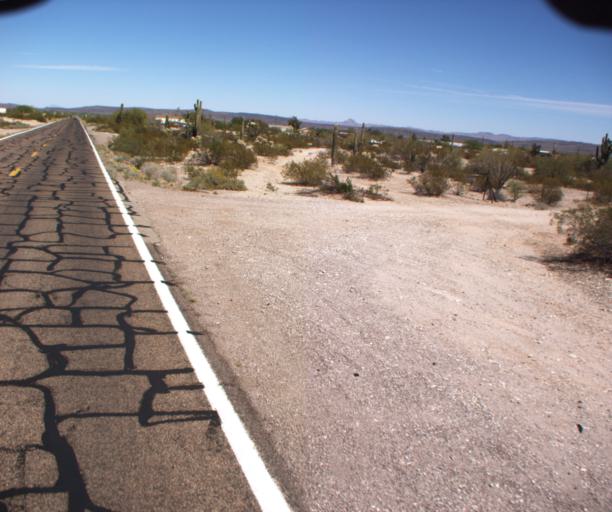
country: US
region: Arizona
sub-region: Pima County
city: Ajo
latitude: 32.4080
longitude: -112.8718
